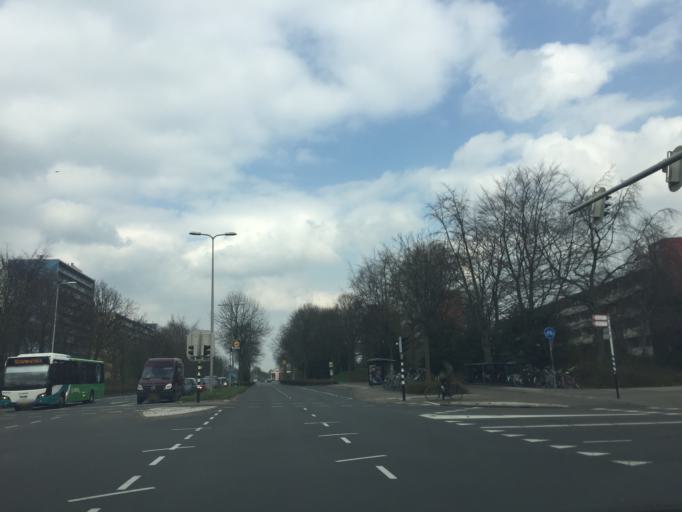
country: NL
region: South Holland
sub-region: Gemeente Alphen aan den Rijn
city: Alphen aan den Rijn
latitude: 52.1458
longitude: 4.6583
